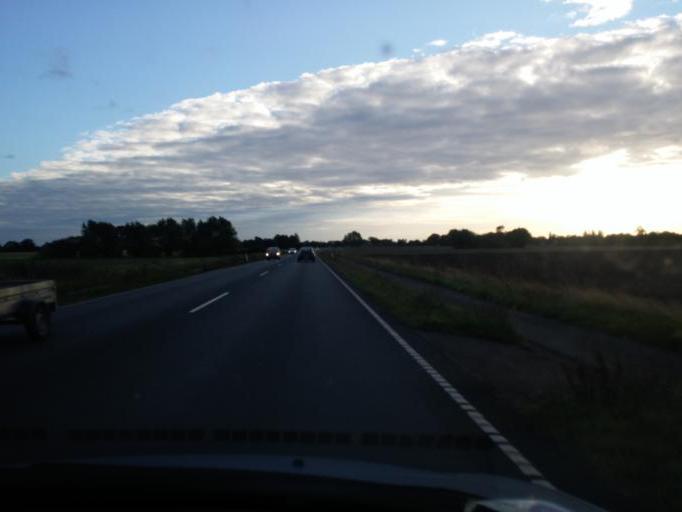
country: DK
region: South Denmark
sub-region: Odense Kommune
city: Bullerup
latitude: 55.4360
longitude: 10.4950
